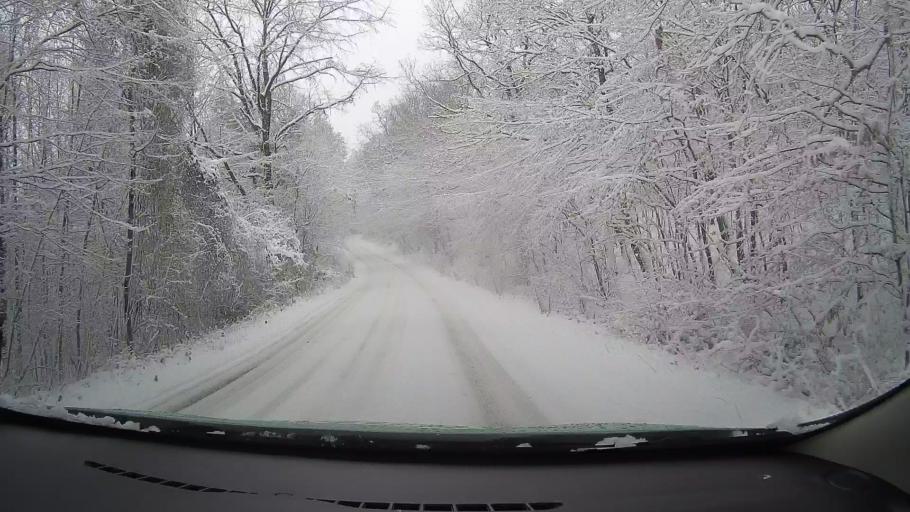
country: RO
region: Hunedoara
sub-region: Municipiul Deva
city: Deva
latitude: 45.8531
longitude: 22.8805
